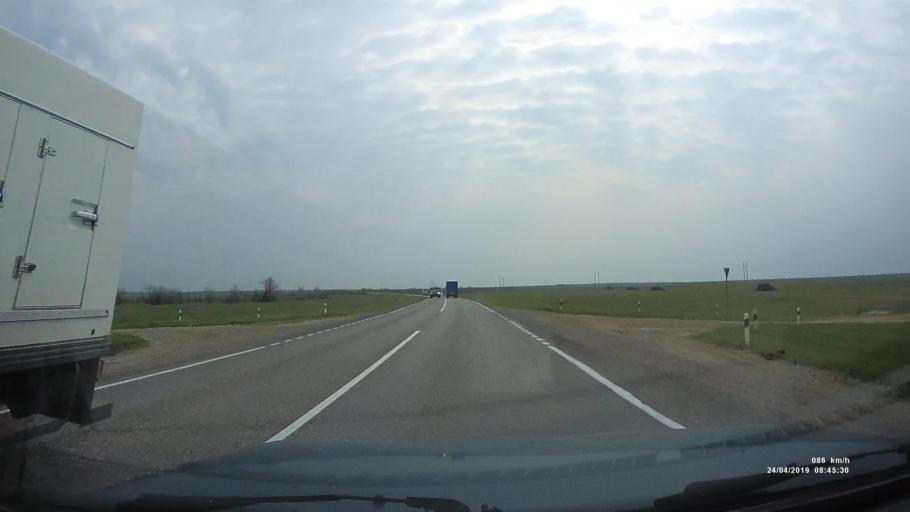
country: RU
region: Kalmykiya
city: Arshan'
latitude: 46.2359
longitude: 44.0631
